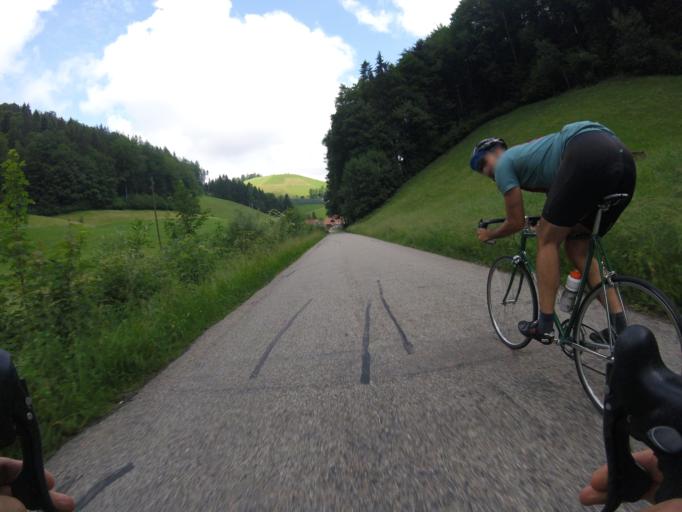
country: CH
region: Bern
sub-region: Emmental District
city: Krauchthal
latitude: 46.9872
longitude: 7.5824
